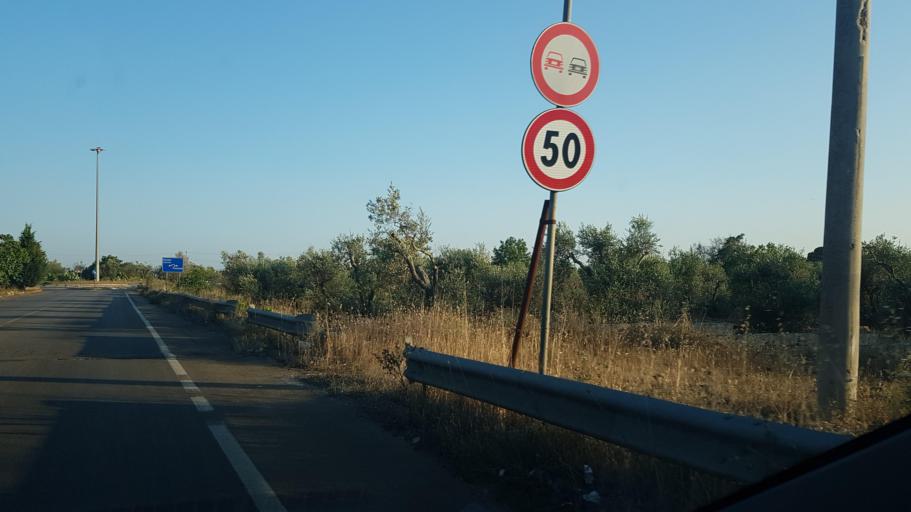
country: IT
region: Apulia
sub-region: Provincia di Lecce
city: Ruffano
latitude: 39.9630
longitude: 18.2579
